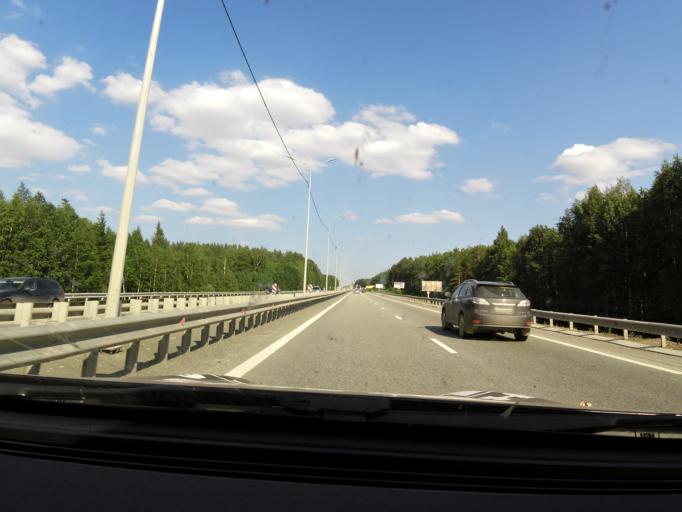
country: RU
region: Sverdlovsk
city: Shirokaya Rechka
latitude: 56.8282
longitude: 60.4233
